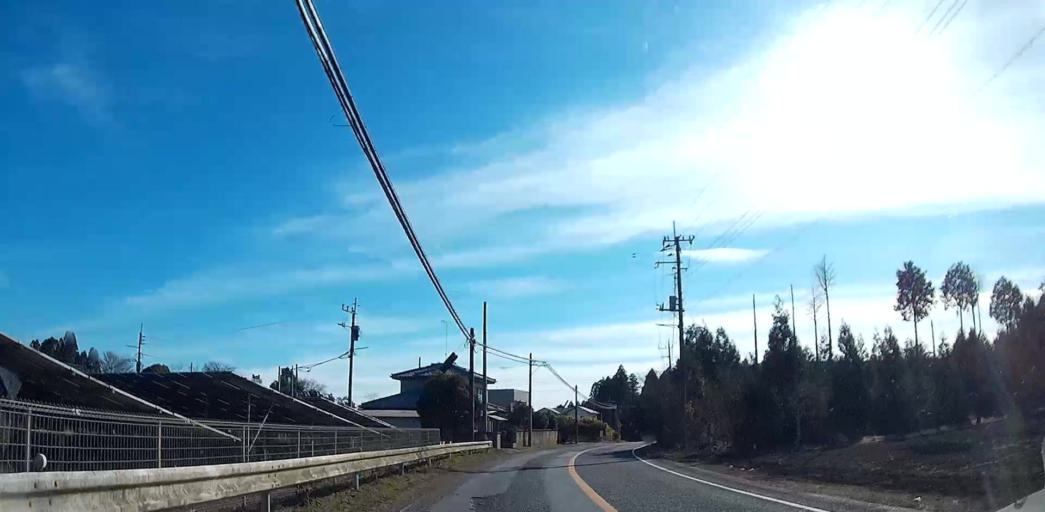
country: JP
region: Chiba
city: Yokaichiba
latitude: 35.7651
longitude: 140.4455
